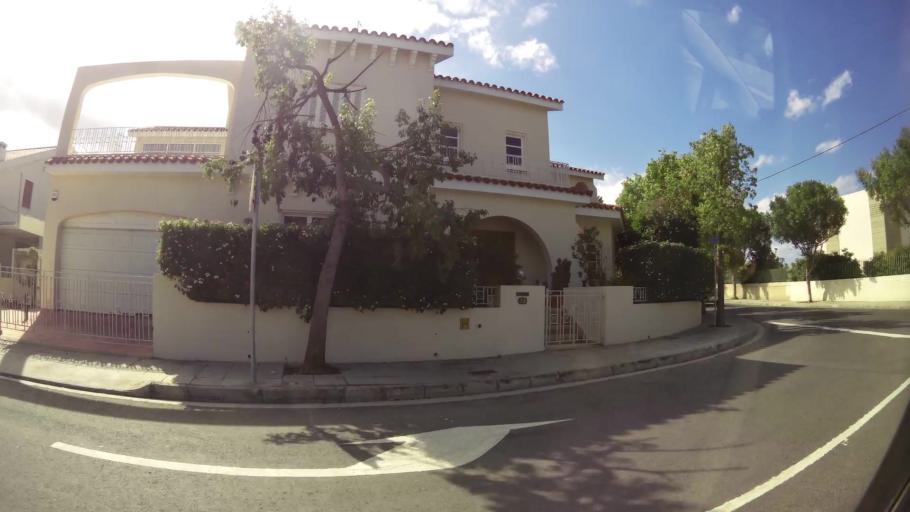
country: CY
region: Lefkosia
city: Nicosia
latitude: 35.1472
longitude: 33.3712
